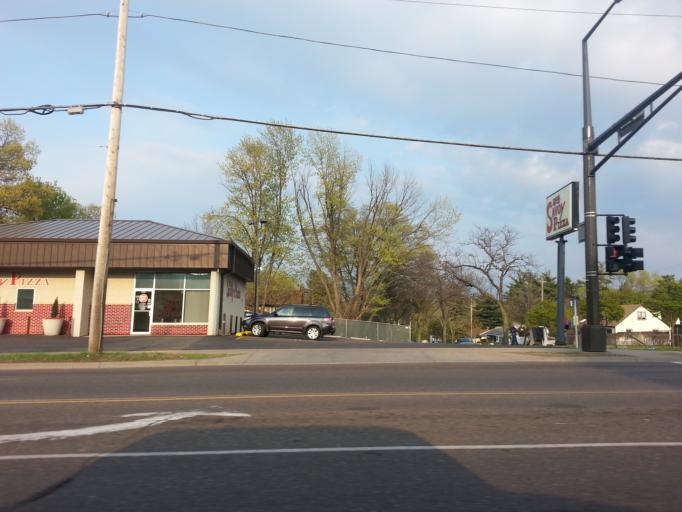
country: US
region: Minnesota
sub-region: Ramsey County
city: Maplewood
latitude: 44.9570
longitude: -93.0253
